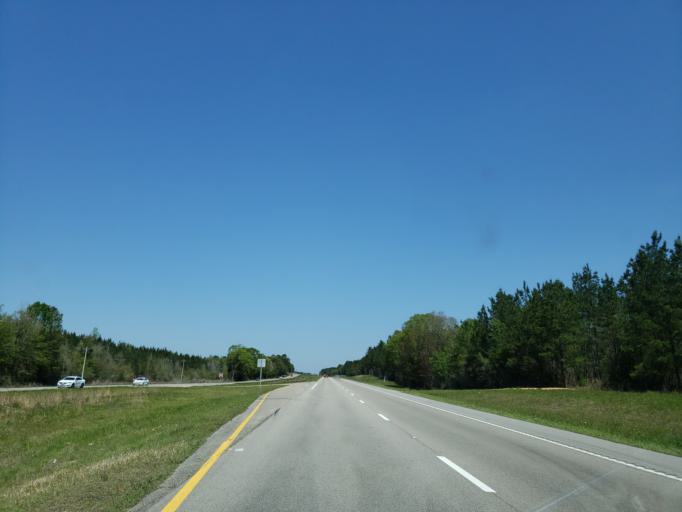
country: US
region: Mississippi
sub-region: Stone County
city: Wiggins
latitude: 30.9931
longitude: -89.2011
